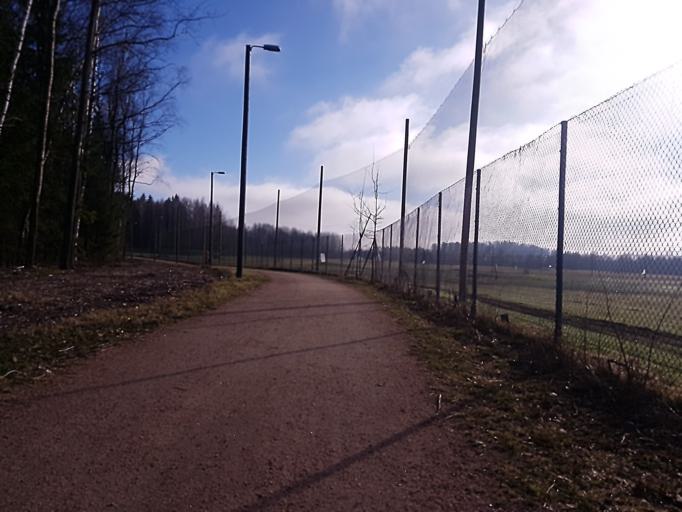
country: FI
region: Uusimaa
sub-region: Helsinki
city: Helsinki
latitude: 60.2576
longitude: 24.9314
